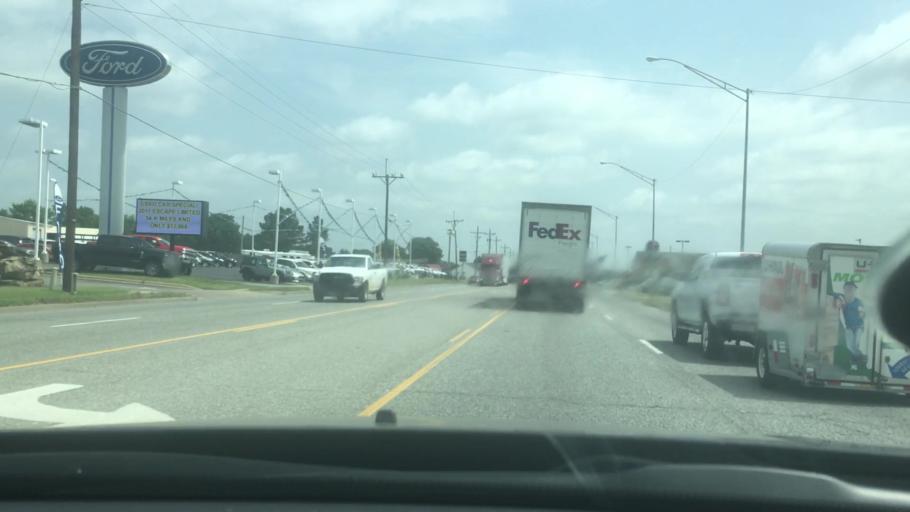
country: US
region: Oklahoma
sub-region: Atoka County
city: Atoka
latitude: 34.3700
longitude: -96.1380
